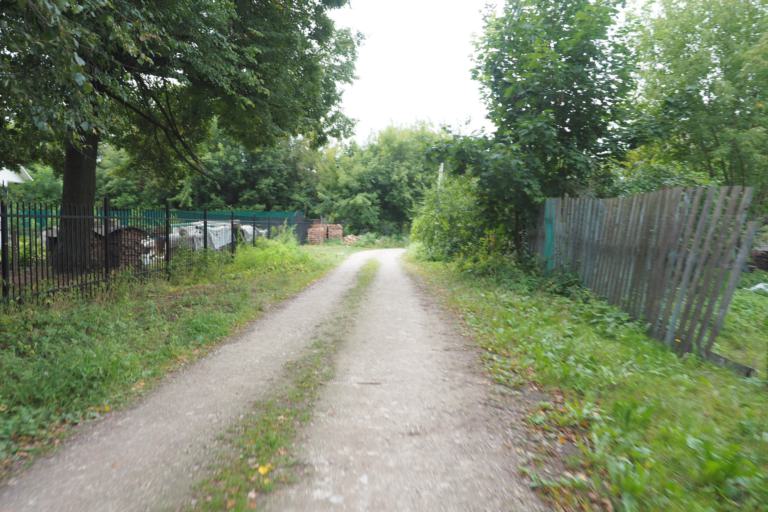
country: RU
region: Moskovskaya
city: Malyshevo
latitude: 55.5384
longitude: 38.3255
